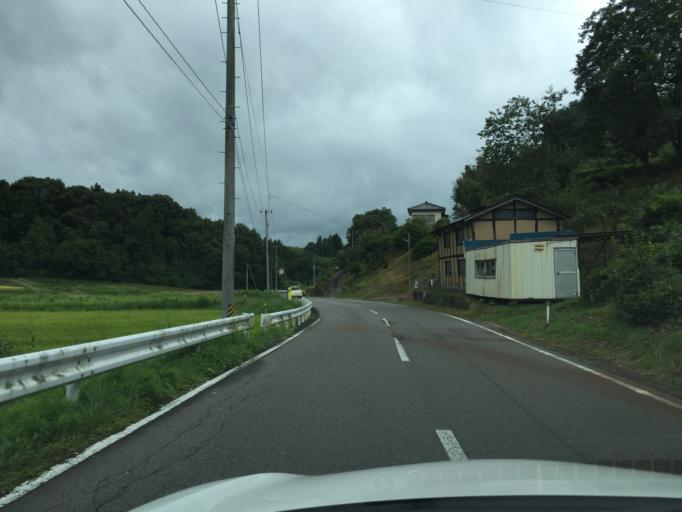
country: JP
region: Fukushima
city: Funehikimachi-funehiki
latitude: 37.4622
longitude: 140.5422
